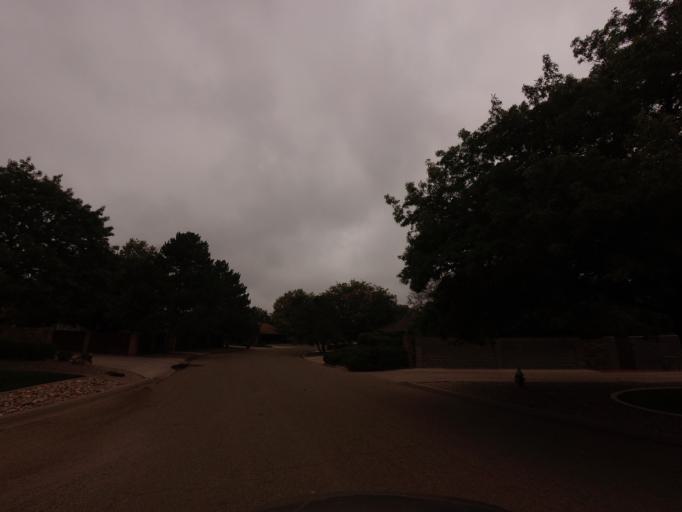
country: US
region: New Mexico
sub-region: Curry County
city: Clovis
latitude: 34.4273
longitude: -103.1807
